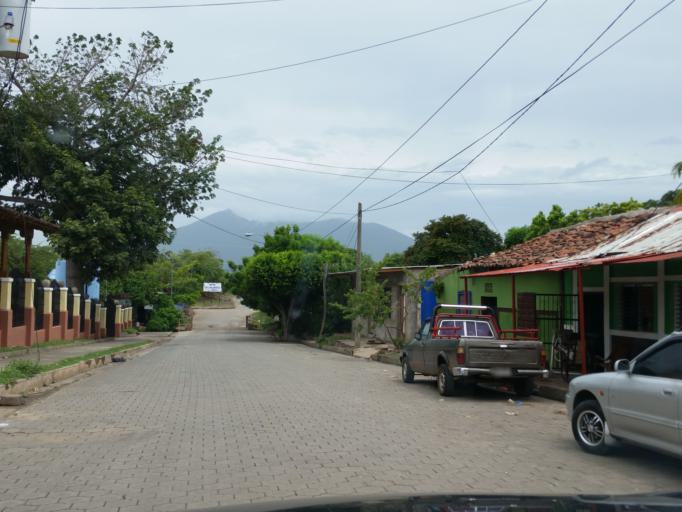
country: NI
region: Granada
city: Granada
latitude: 11.9361
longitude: -85.9601
